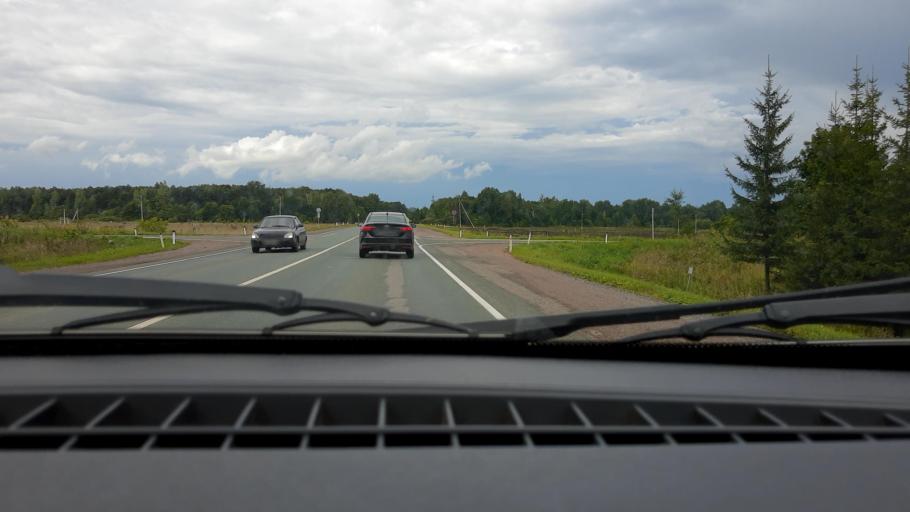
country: RU
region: Bashkortostan
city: Avdon
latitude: 54.8127
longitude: 55.7364
